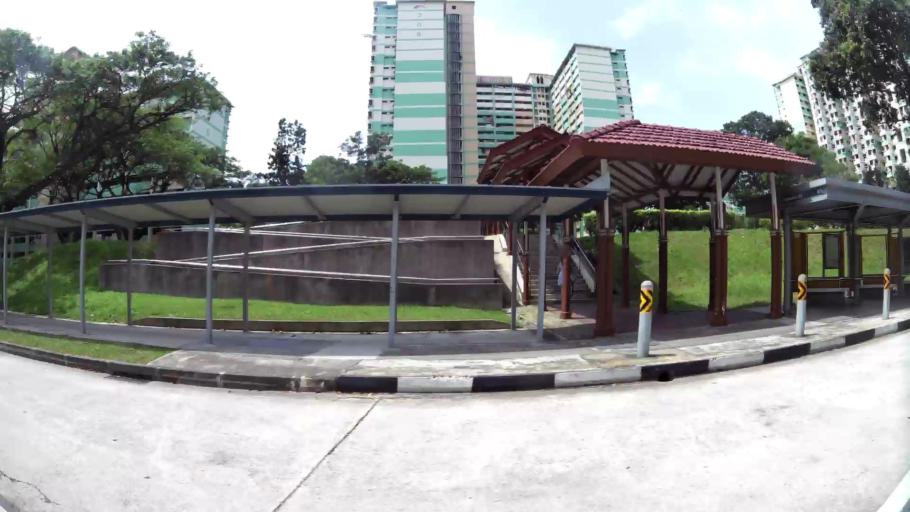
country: MY
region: Johor
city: Johor Bahru
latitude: 1.3477
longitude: 103.7151
